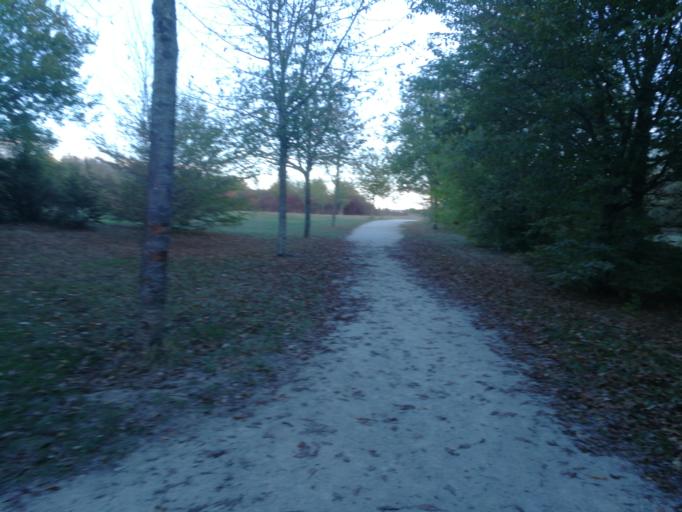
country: FR
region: Centre
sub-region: Departement d'Indre-et-Loire
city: Chanceaux-sur-Choisille
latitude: 47.4416
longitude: 0.6889
